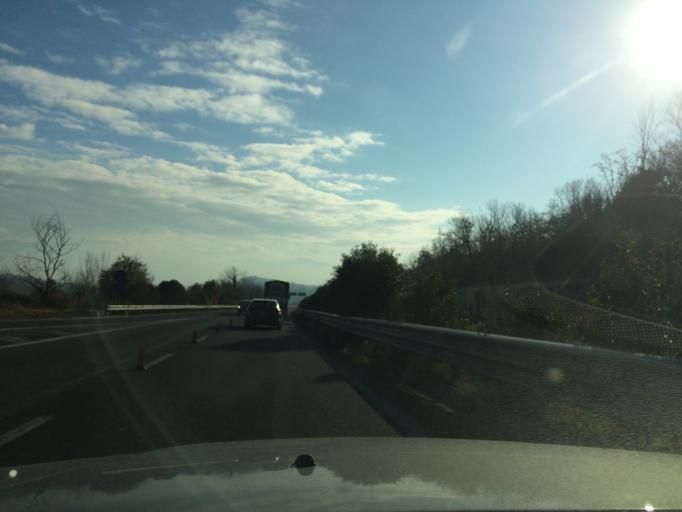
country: IT
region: Umbria
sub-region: Provincia di Terni
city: San Gemini
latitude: 42.6190
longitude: 12.5534
